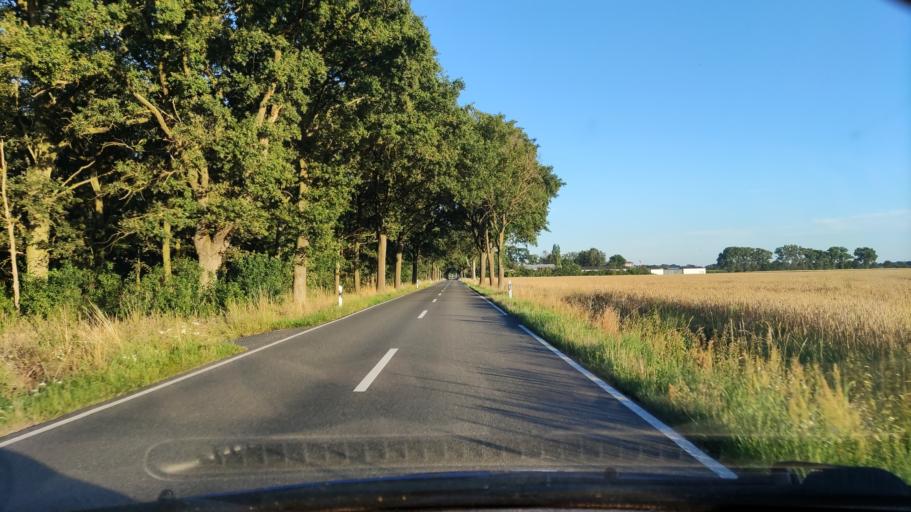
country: DE
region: Lower Saxony
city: Luechow
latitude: 53.0200
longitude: 11.1461
